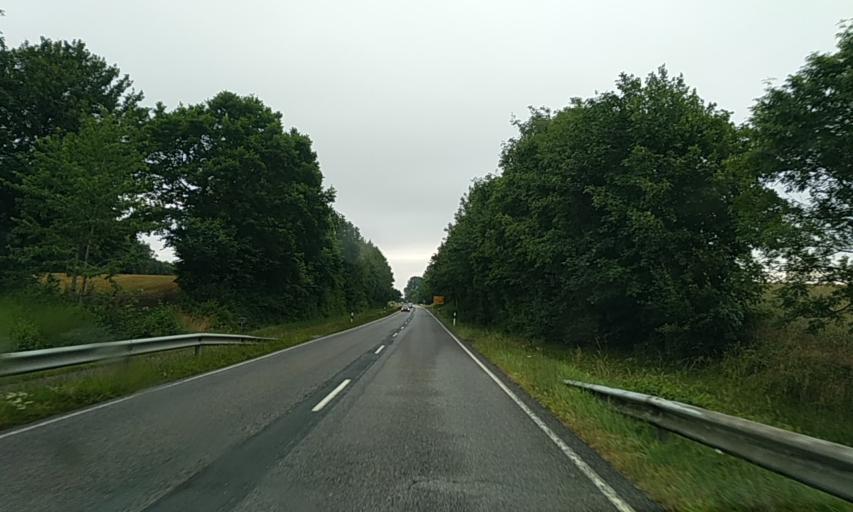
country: DE
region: Schleswig-Holstein
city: Ulsby
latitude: 54.6196
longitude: 9.6201
